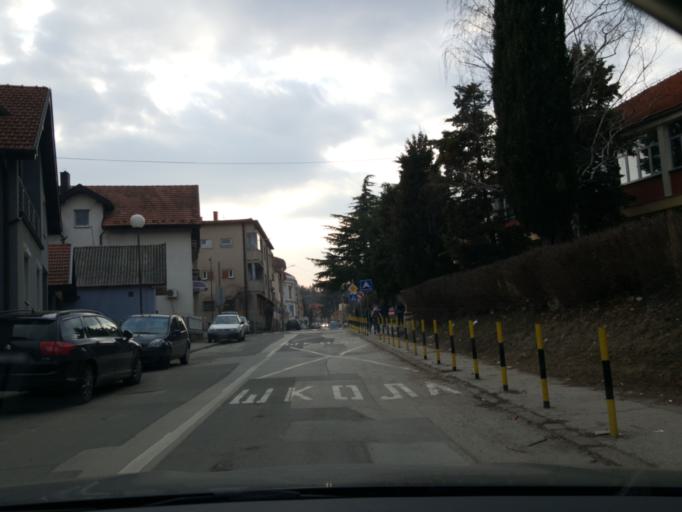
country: RS
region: Central Serbia
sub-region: Nisavski Okrug
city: Aleksinac
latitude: 43.5423
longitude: 21.7101
